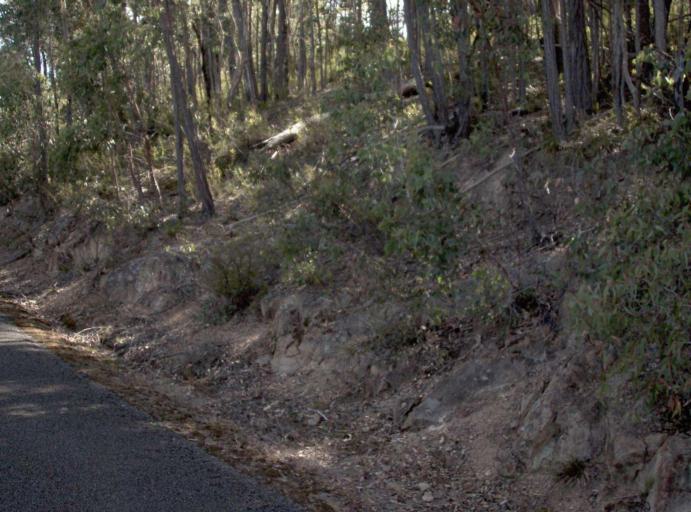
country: AU
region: Victoria
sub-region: East Gippsland
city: Lakes Entrance
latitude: -37.4792
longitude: 148.1240
